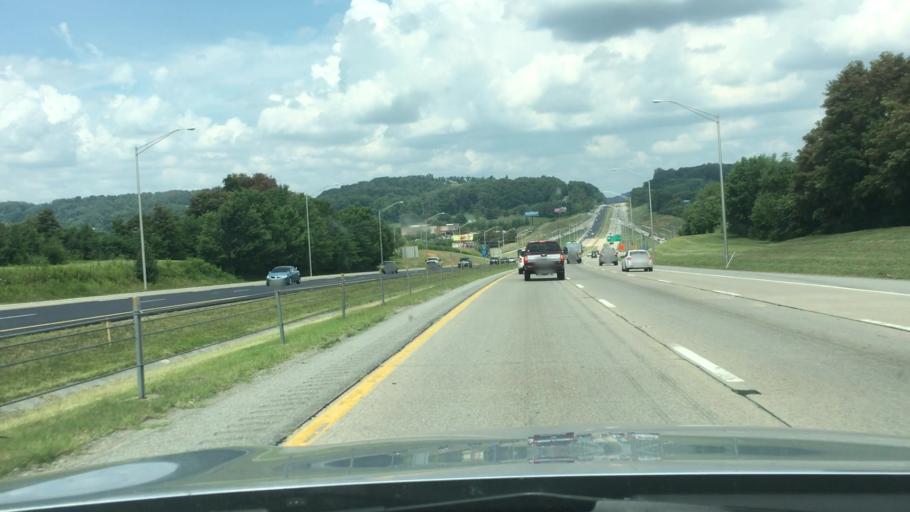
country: US
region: Tennessee
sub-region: Washington County
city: Johnson City
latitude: 36.3520
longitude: -82.3903
